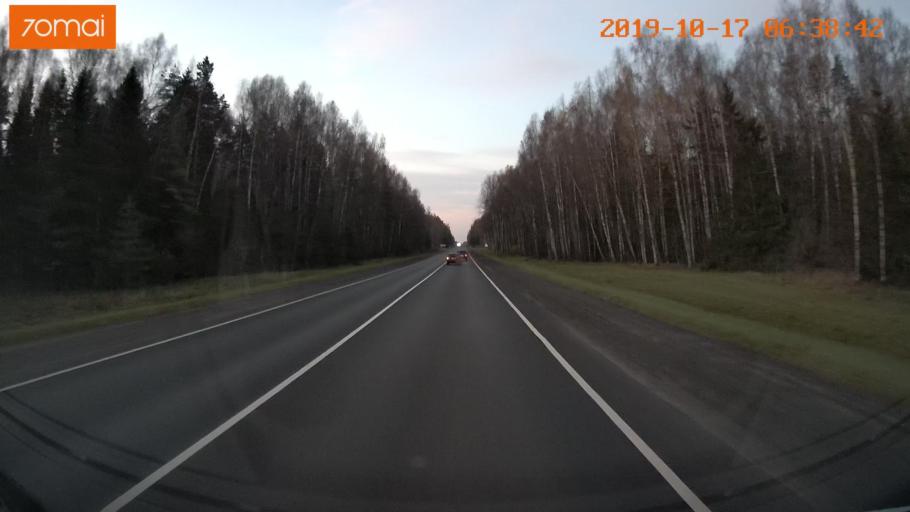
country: RU
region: Ivanovo
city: Novoye Leushino
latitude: 56.6525
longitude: 40.5851
